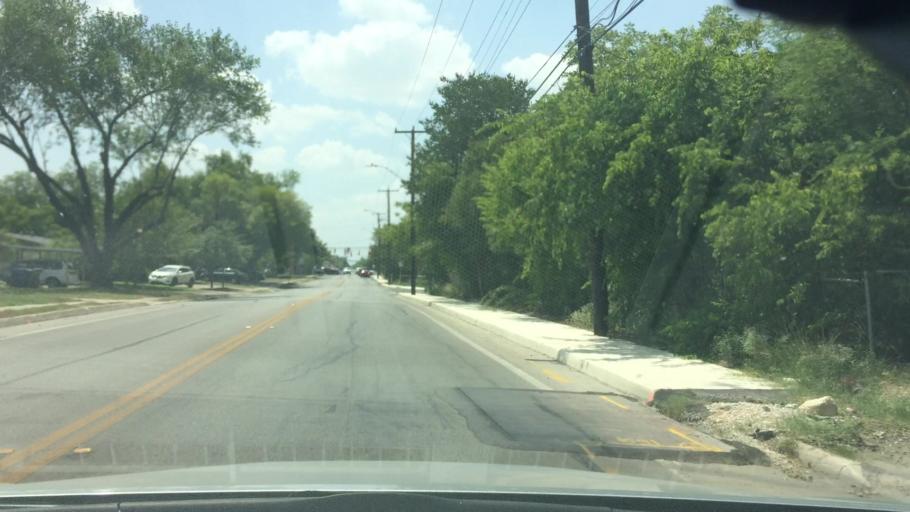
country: US
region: Texas
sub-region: Bexar County
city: Olmos Park
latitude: 29.5043
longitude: -98.4897
